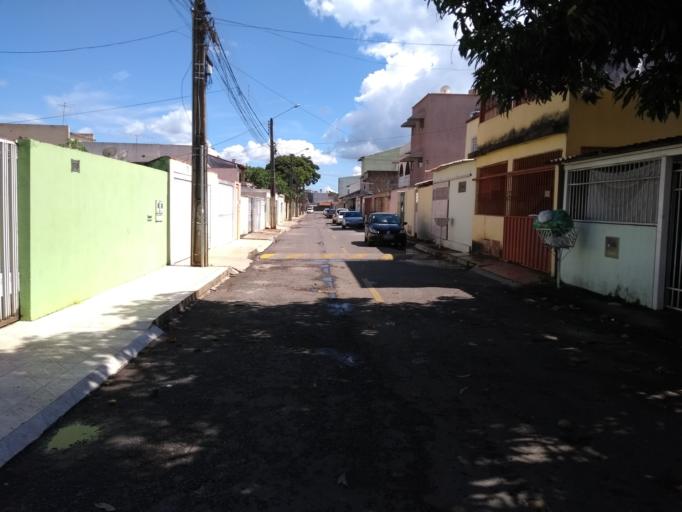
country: BR
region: Federal District
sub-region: Brasilia
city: Brasilia
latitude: -15.7907
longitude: -47.9407
